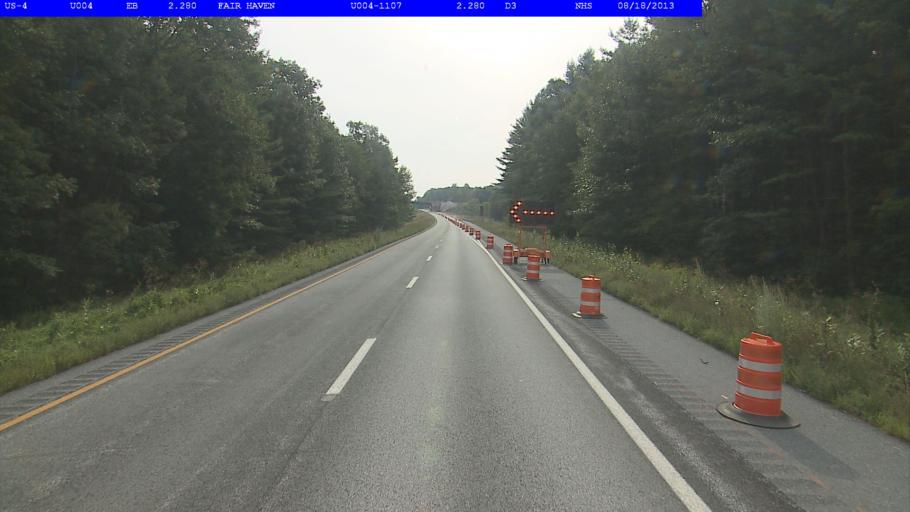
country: US
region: Vermont
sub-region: Rutland County
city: Fair Haven
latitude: 43.6052
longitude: -73.2659
